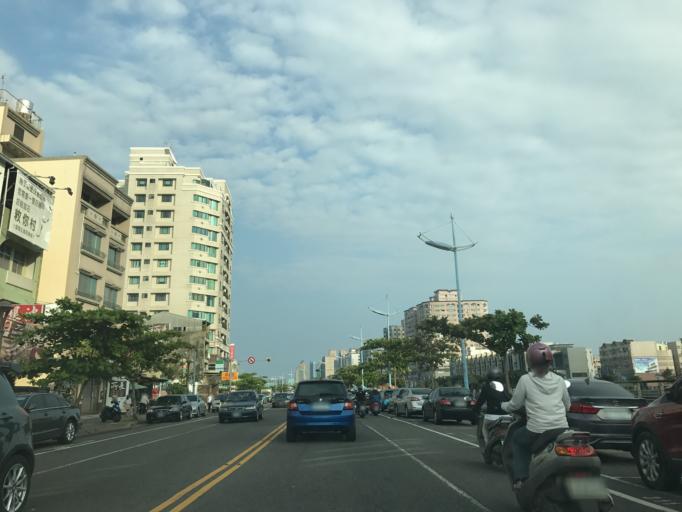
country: TW
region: Taiwan
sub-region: Tainan
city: Tainan
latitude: 22.9981
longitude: 120.1729
